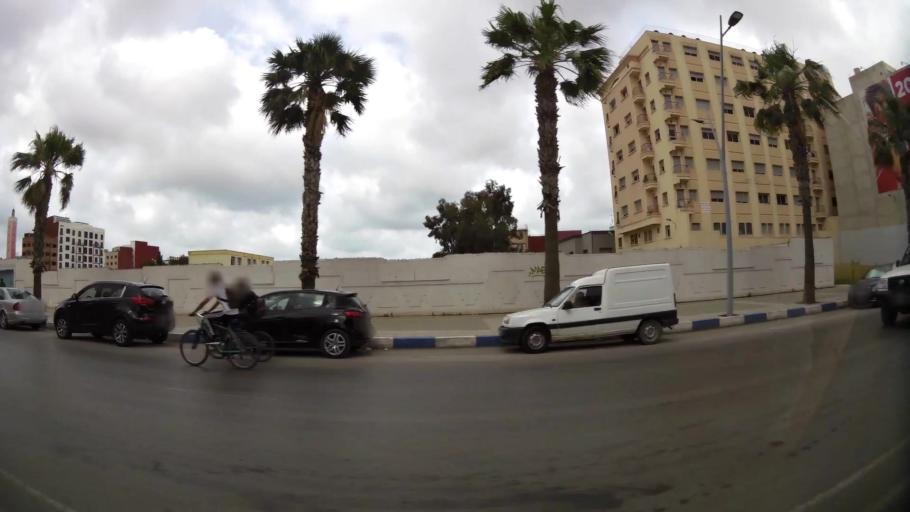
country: MA
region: Oriental
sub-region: Nador
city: Nador
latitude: 35.1595
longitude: -2.9306
